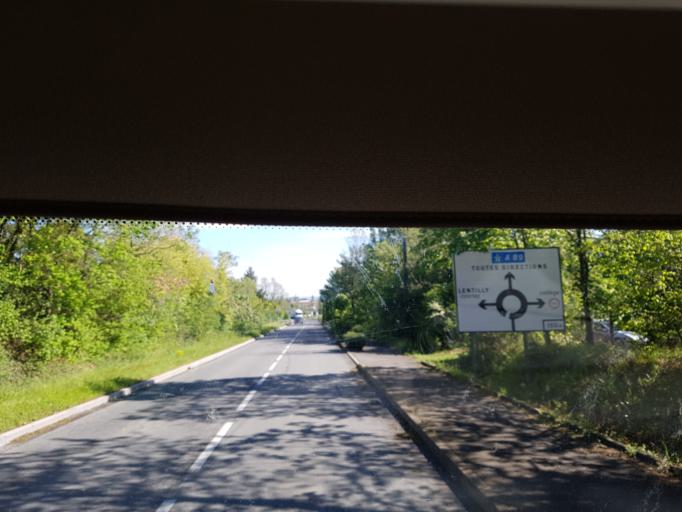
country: FR
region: Rhone-Alpes
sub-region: Departement du Rhone
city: Lentilly
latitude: 45.8156
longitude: 4.6634
